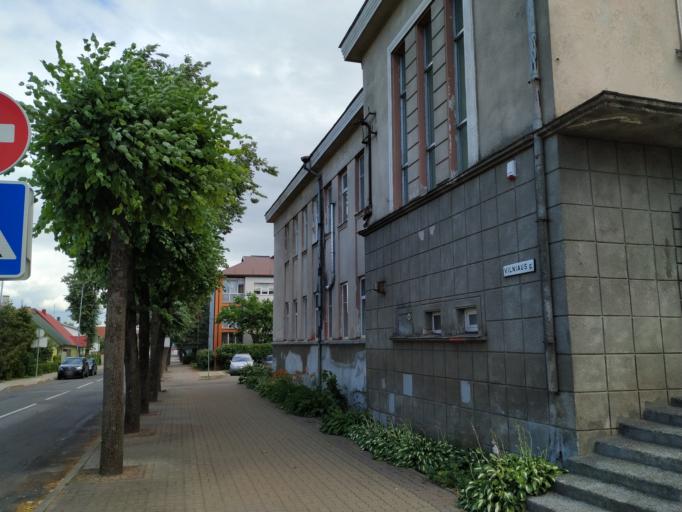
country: LT
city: Kupiskis
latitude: 55.8399
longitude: 24.9764
